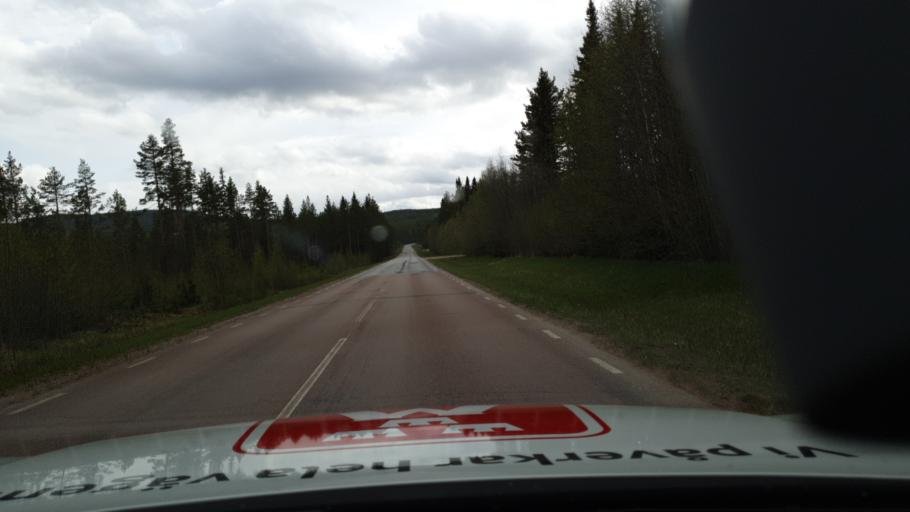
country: SE
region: Jaemtland
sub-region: Braecke Kommun
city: Braecke
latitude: 62.8638
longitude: 15.5809
